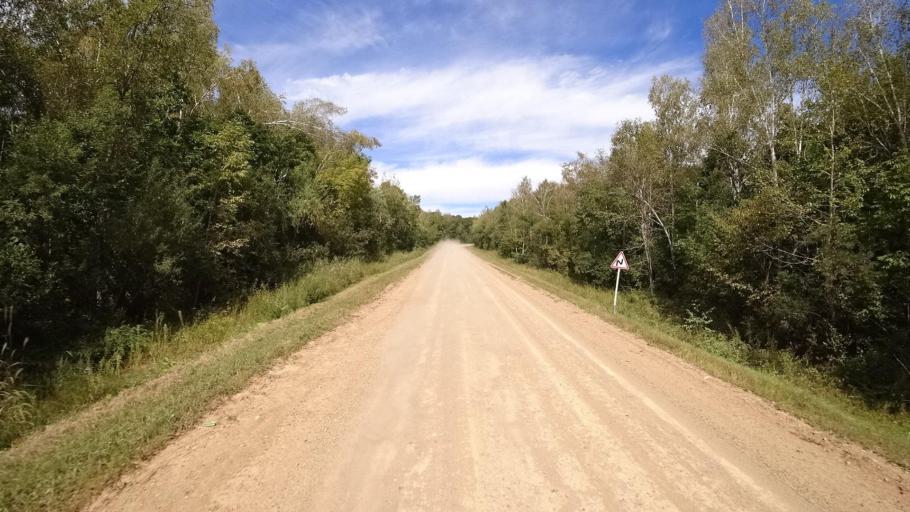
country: RU
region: Primorskiy
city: Yakovlevka
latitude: 44.6570
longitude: 133.5967
